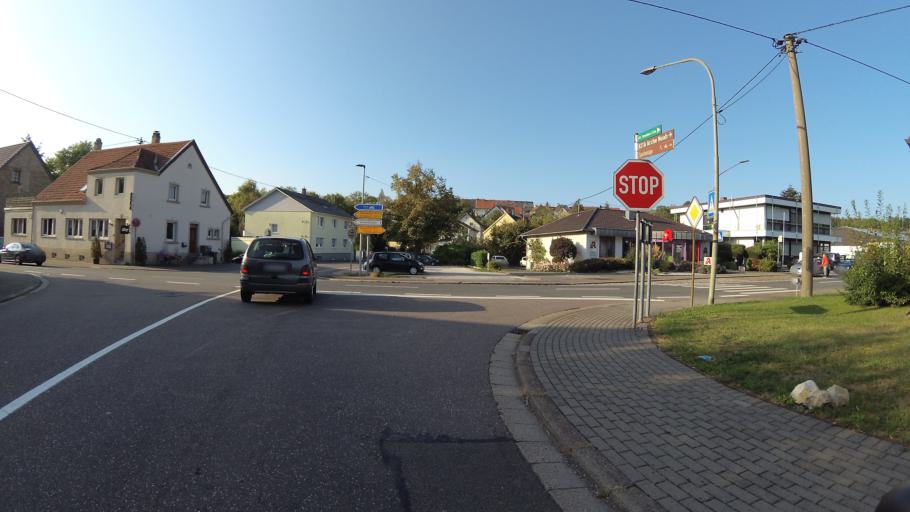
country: DE
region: Saarland
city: Sankt Ingbert
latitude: 49.2166
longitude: 7.1588
